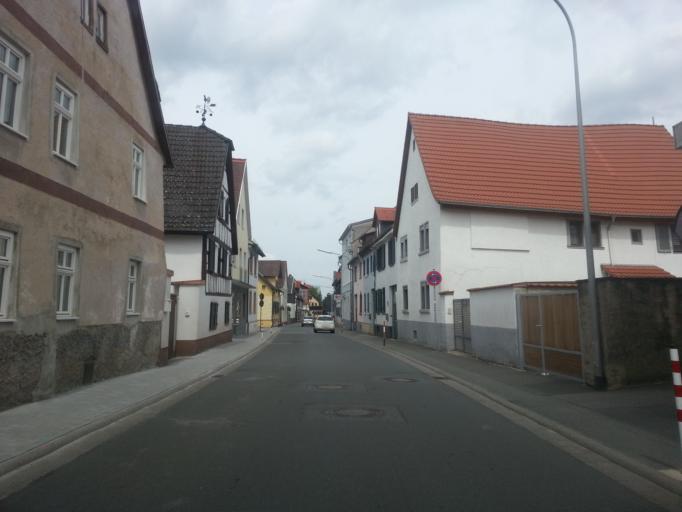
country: DE
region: Hesse
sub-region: Regierungsbezirk Darmstadt
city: Seeheim-Jugenheim
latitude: 49.7660
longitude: 8.6486
